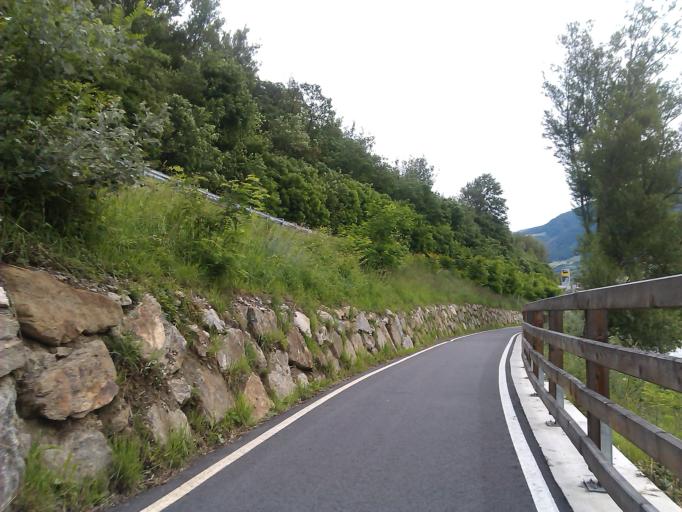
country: IT
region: Trentino-Alto Adige
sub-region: Bolzano
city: Laces
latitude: 46.6228
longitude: 10.8601
